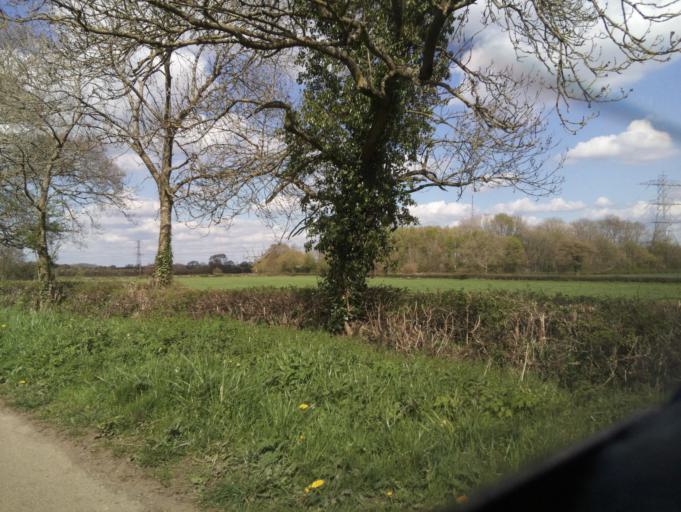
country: GB
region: England
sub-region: South Gloucestershire
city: Tytherington
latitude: 51.5683
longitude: -2.4857
